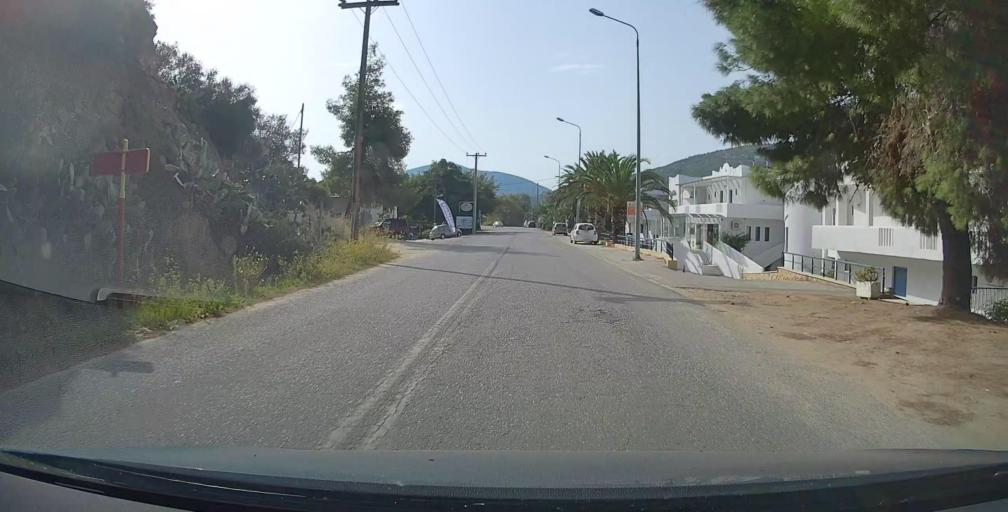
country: GR
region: Central Macedonia
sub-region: Nomos Chalkidikis
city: Sykia
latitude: 39.9639
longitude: 23.9266
